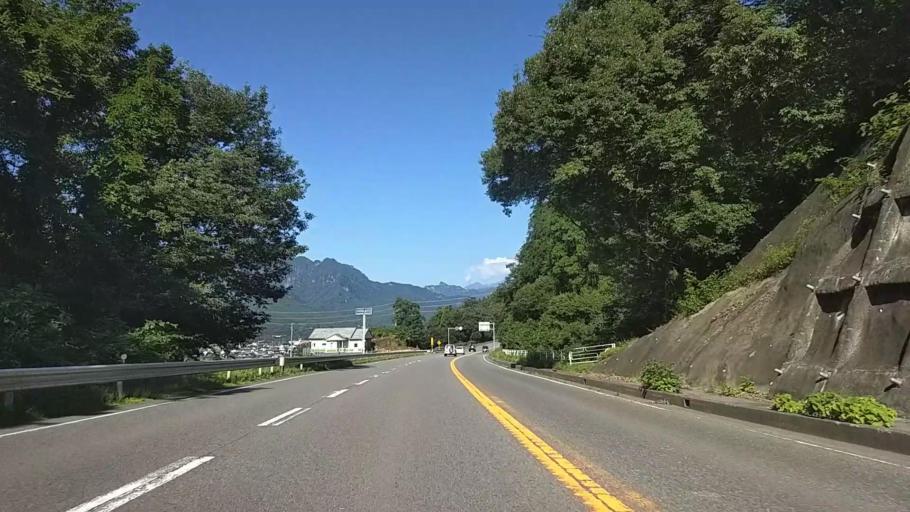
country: JP
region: Gunma
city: Annaka
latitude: 36.3173
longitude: 138.7990
